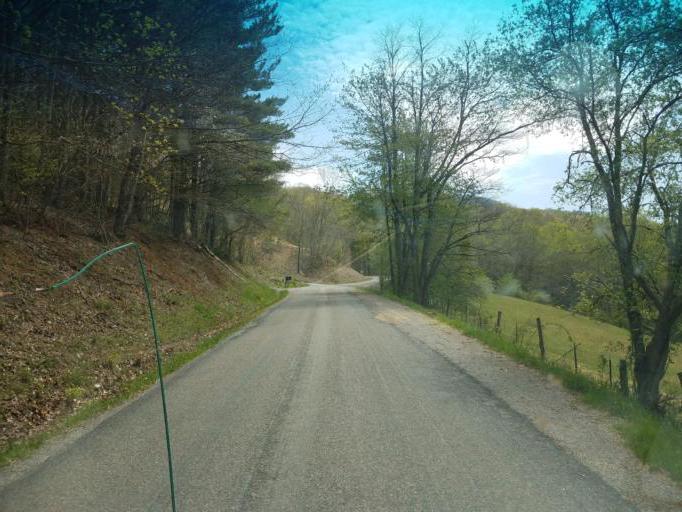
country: US
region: Virginia
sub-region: Smyth County
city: Marion
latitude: 36.7985
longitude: -81.4641
